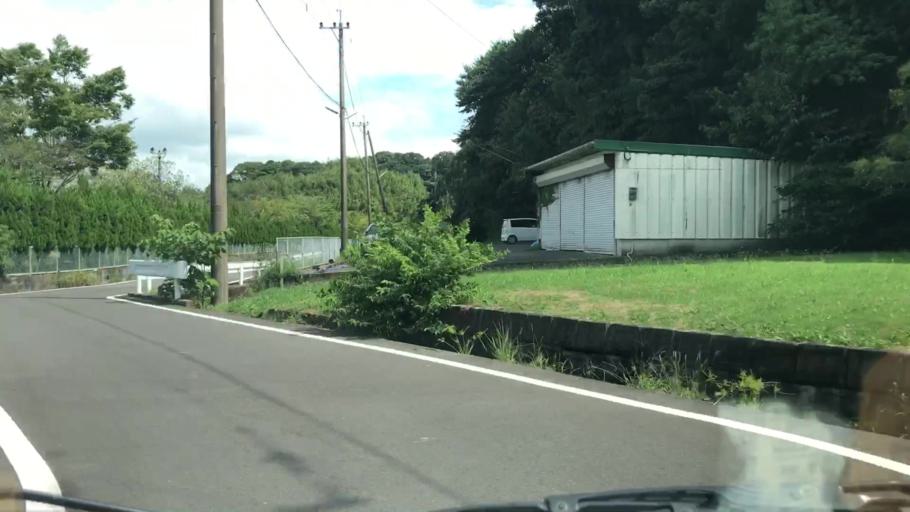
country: JP
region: Saga Prefecture
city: Saga-shi
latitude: 33.2302
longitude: 130.1764
